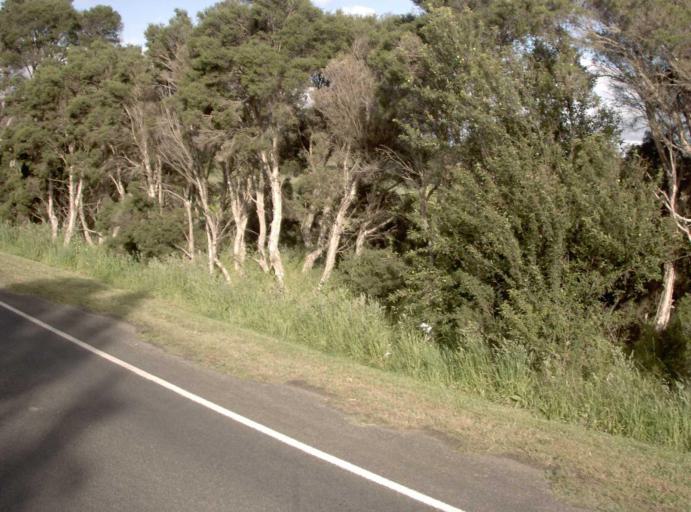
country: AU
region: Victoria
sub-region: Baw Baw
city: Warragul
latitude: -38.4905
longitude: 145.9311
